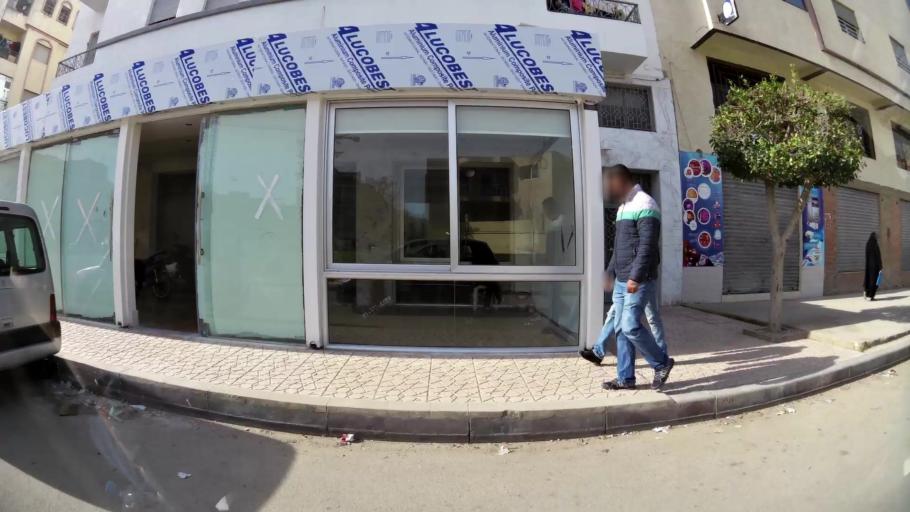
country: MA
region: Tanger-Tetouan
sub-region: Tanger-Assilah
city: Tangier
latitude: 35.7430
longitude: -5.7975
